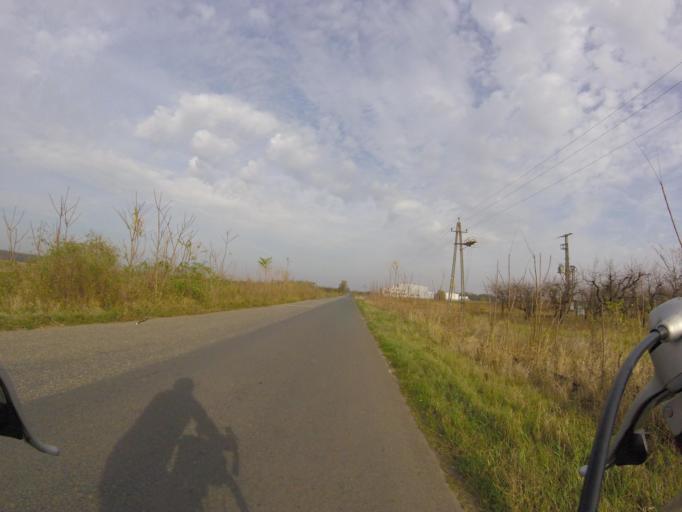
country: HU
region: Bacs-Kiskun
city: Lajosmizse
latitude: 47.0546
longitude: 19.5223
